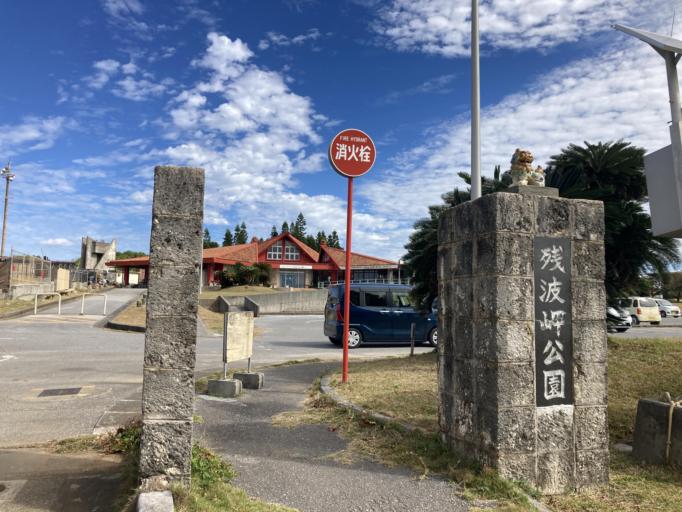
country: JP
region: Okinawa
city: Ishikawa
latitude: 26.4384
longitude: 127.7143
